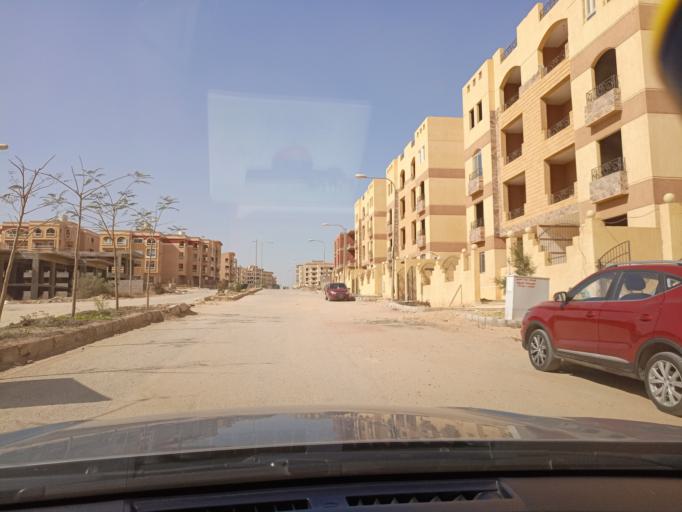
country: EG
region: Muhafazat al Qalyubiyah
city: Al Khankah
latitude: 30.2184
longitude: 31.4419
